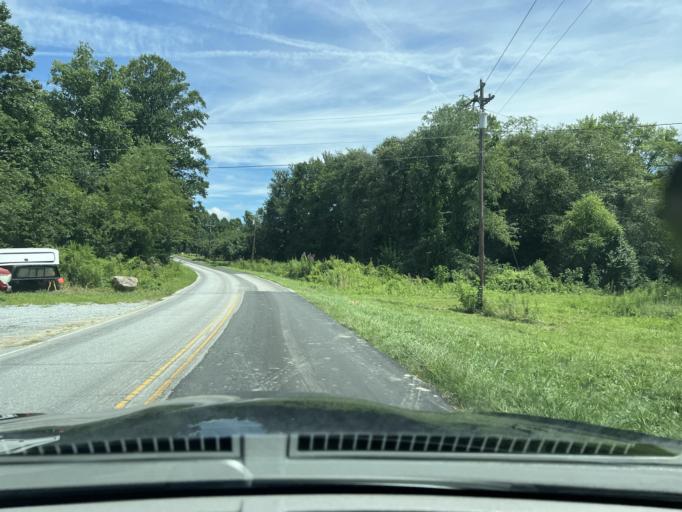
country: US
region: North Carolina
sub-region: Henderson County
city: Edneyville
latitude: 35.3890
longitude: -82.3599
